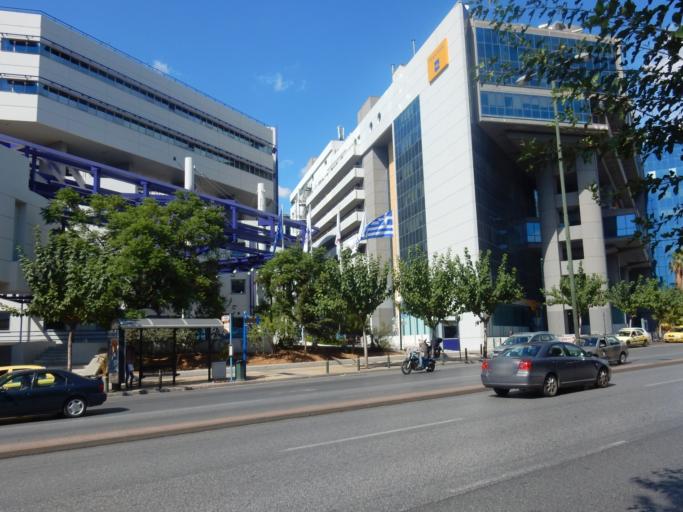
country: GR
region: Attica
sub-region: Nomarchia Athinas
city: Neo Psychiko
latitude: 37.9899
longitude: 23.7703
